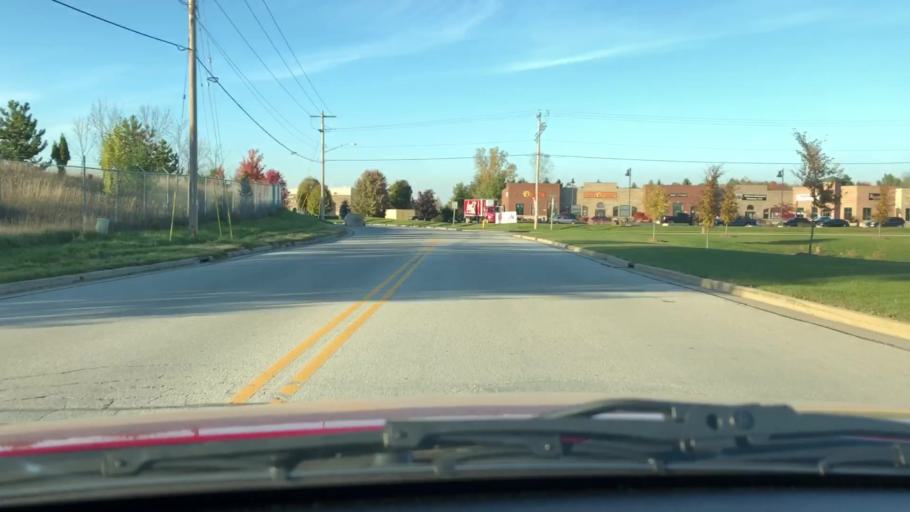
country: US
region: Wisconsin
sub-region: Brown County
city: De Pere
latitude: 44.4304
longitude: -88.1248
